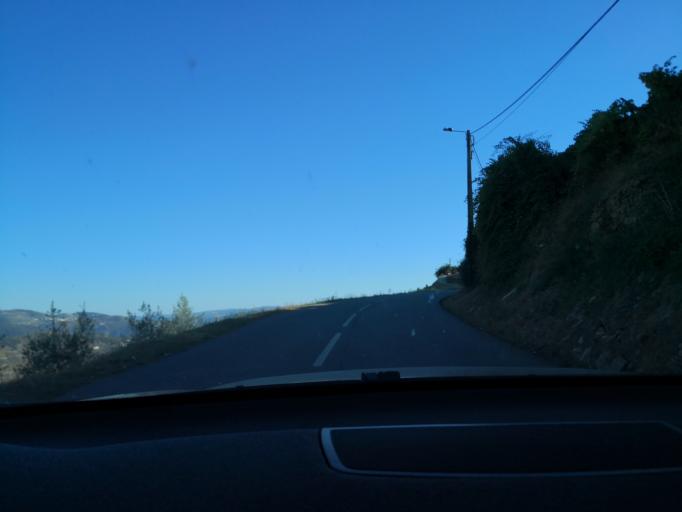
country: PT
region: Vila Real
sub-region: Sabrosa
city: Vilela
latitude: 41.2233
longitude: -7.5627
